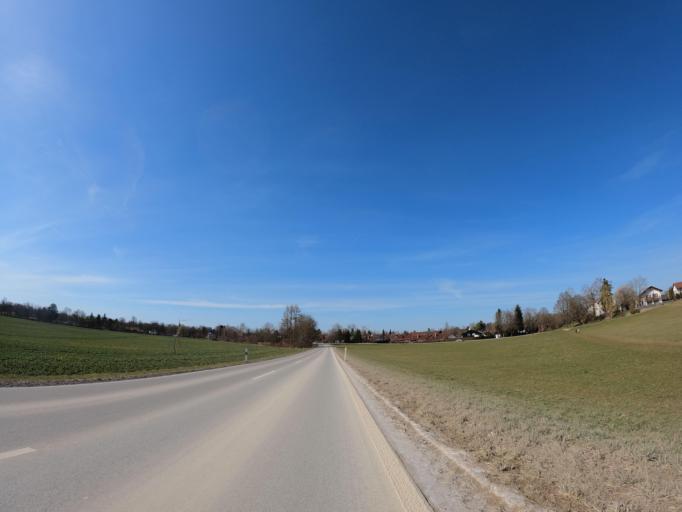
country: DE
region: Bavaria
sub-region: Upper Bavaria
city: Oberhaching
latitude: 48.0220
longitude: 11.6013
